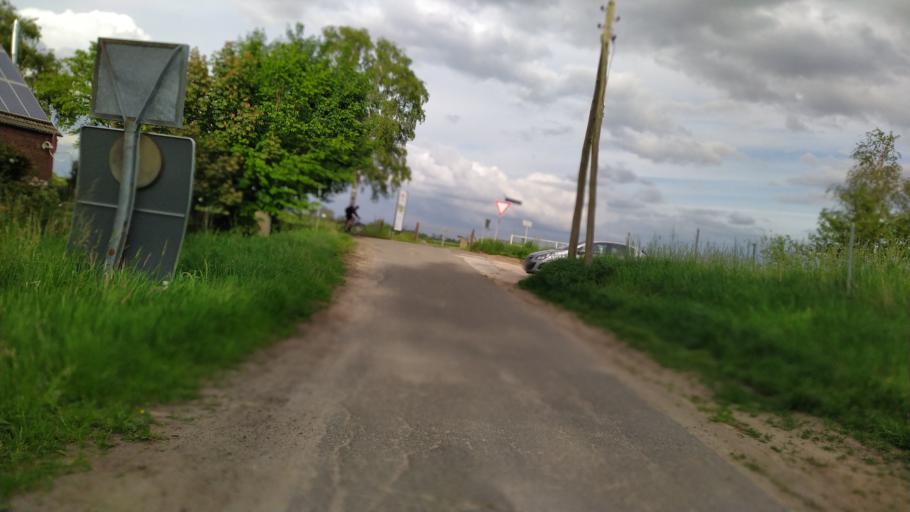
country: DE
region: Lower Saxony
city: Neu Wulmstorf
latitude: 53.4958
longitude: 9.8724
